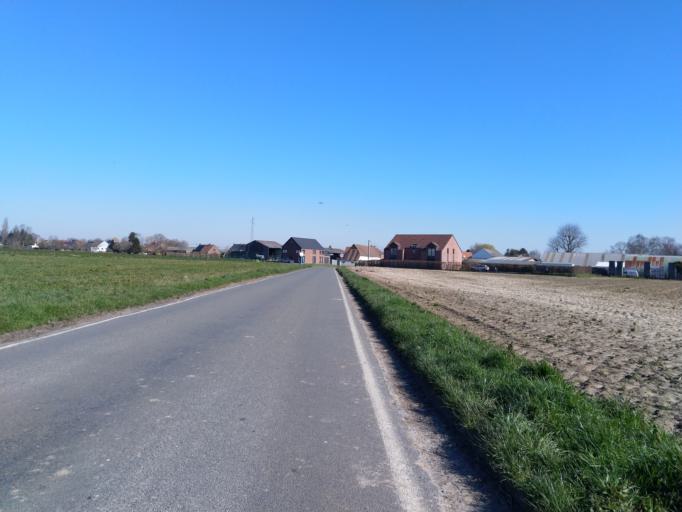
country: BE
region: Wallonia
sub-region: Province du Hainaut
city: Lens
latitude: 50.5424
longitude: 3.8584
